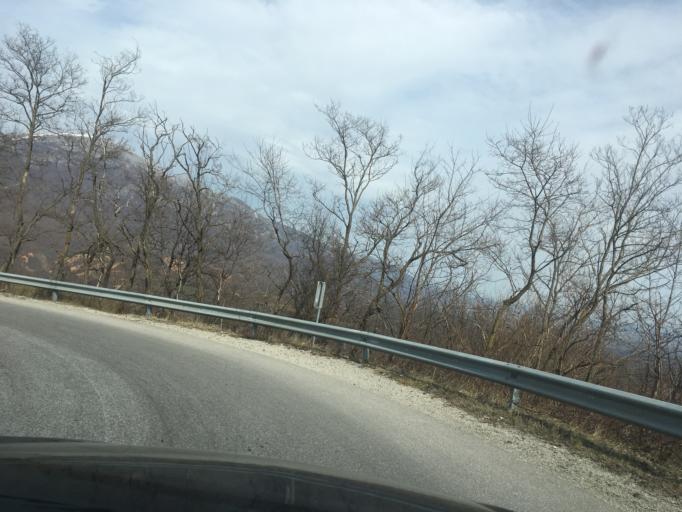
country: XK
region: Pec
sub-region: Komuna e Pejes
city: Dubova (Driloni)
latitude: 42.7491
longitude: 20.3082
